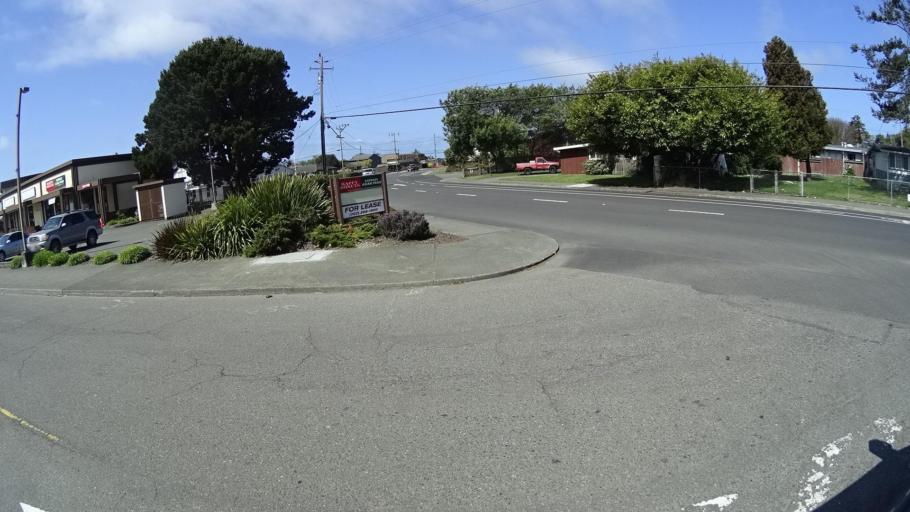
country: US
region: California
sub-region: Humboldt County
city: Bayview
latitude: 40.7814
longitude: -124.1809
